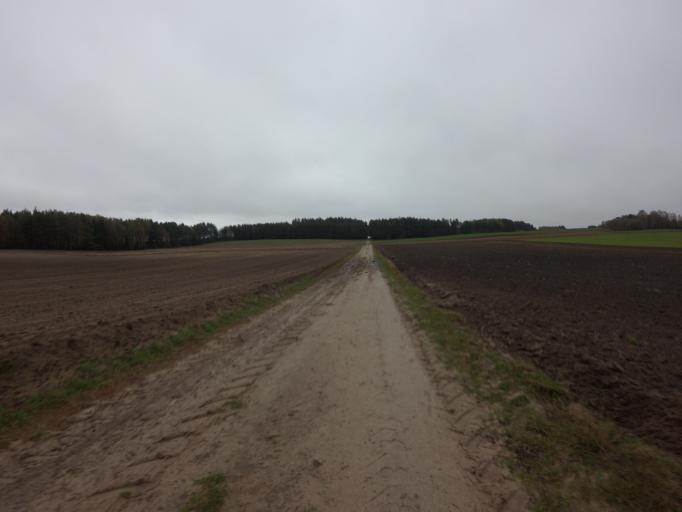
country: PL
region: Pomeranian Voivodeship
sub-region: Powiat kartuski
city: Stezyca
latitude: 54.1698
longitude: 17.9357
